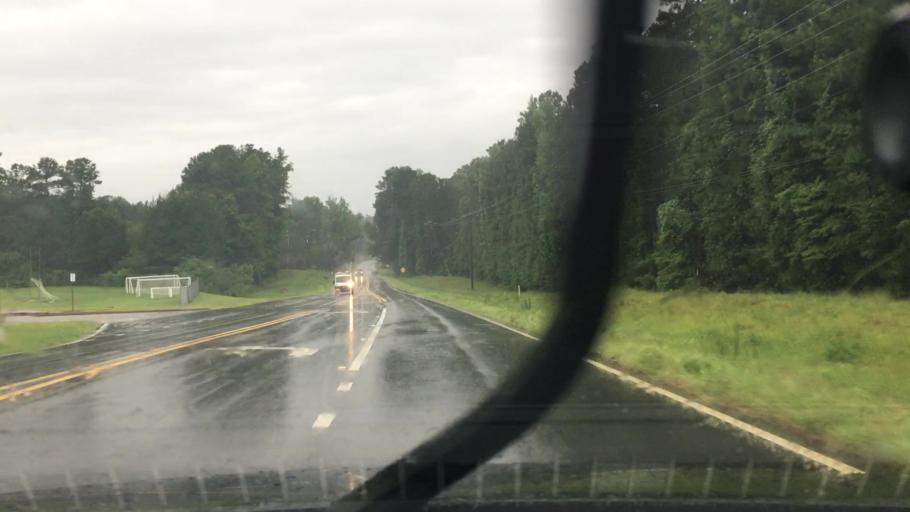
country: US
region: Georgia
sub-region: Coweta County
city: East Newnan
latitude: 33.3442
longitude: -84.6901
